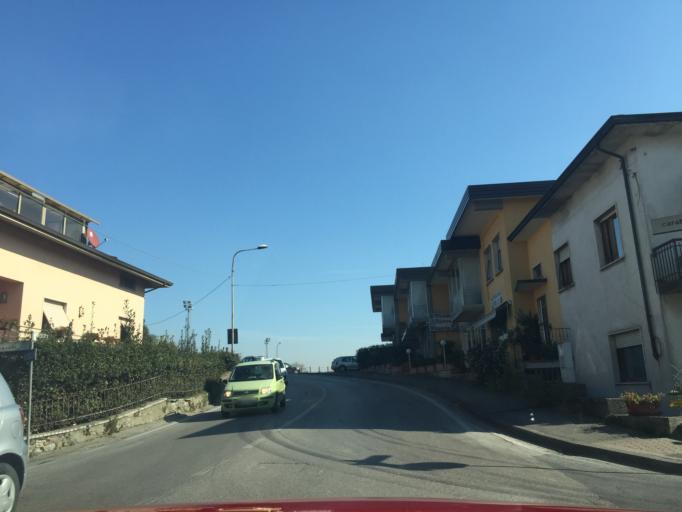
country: IT
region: Tuscany
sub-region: Provincia di Pistoia
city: Ponte Buggianese
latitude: 43.8395
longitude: 10.7478
